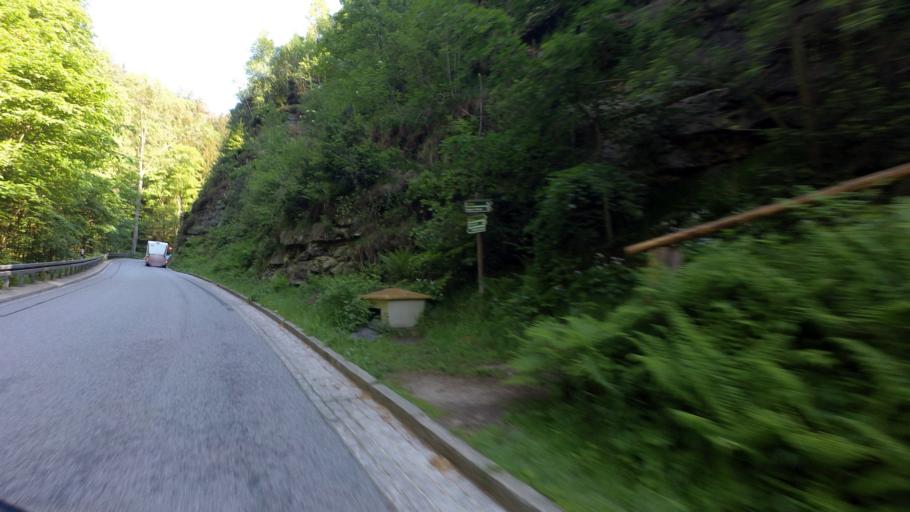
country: DE
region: Saxony
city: Porschdorf
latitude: 50.9565
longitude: 14.1316
